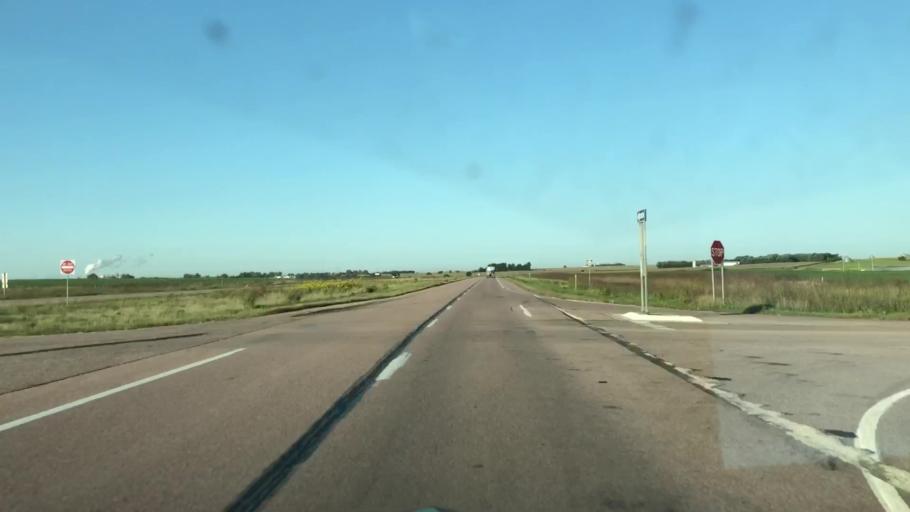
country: US
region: Iowa
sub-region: Osceola County
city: Sibley
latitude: 43.3035
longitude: -95.7843
